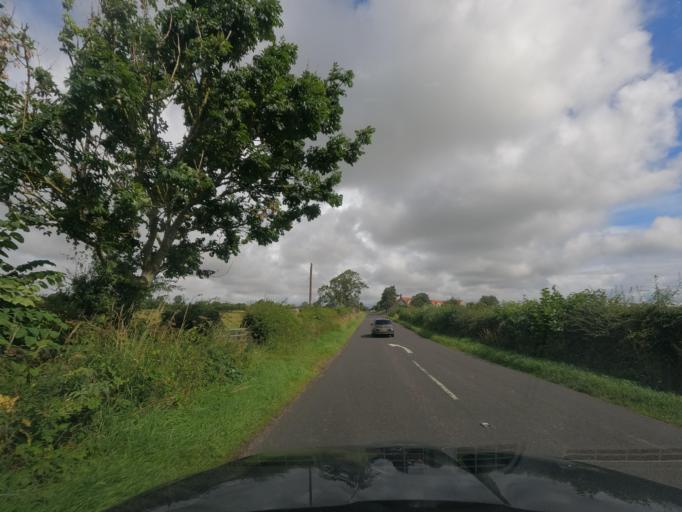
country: GB
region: England
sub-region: Northumberland
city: Lowick
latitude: 55.6232
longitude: -1.9883
